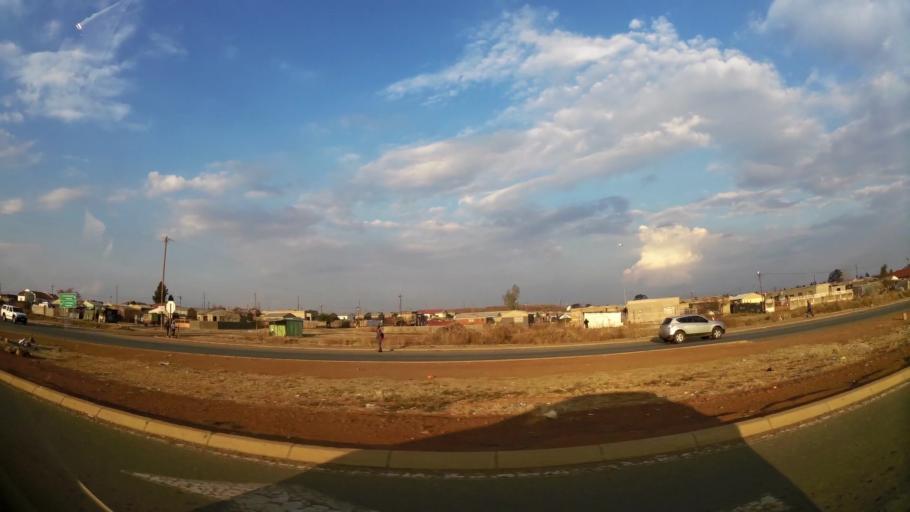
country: ZA
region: Gauteng
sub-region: Sedibeng District Municipality
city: Vanderbijlpark
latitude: -26.6023
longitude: 27.8180
